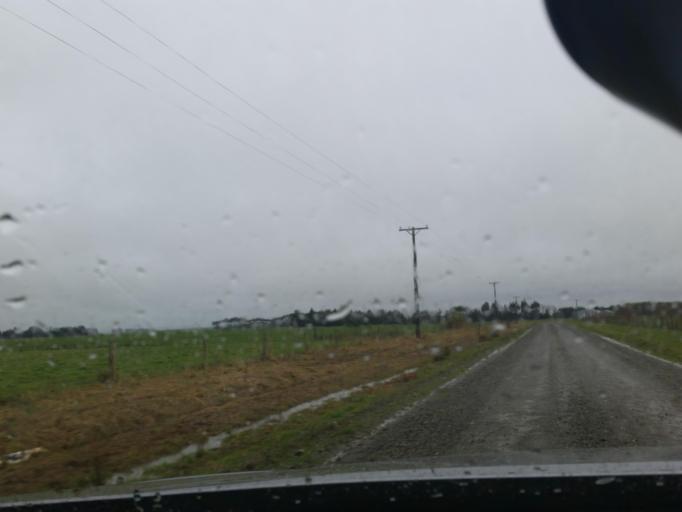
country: NZ
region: Southland
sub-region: Southland District
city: Winton
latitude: -46.1917
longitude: 168.2378
